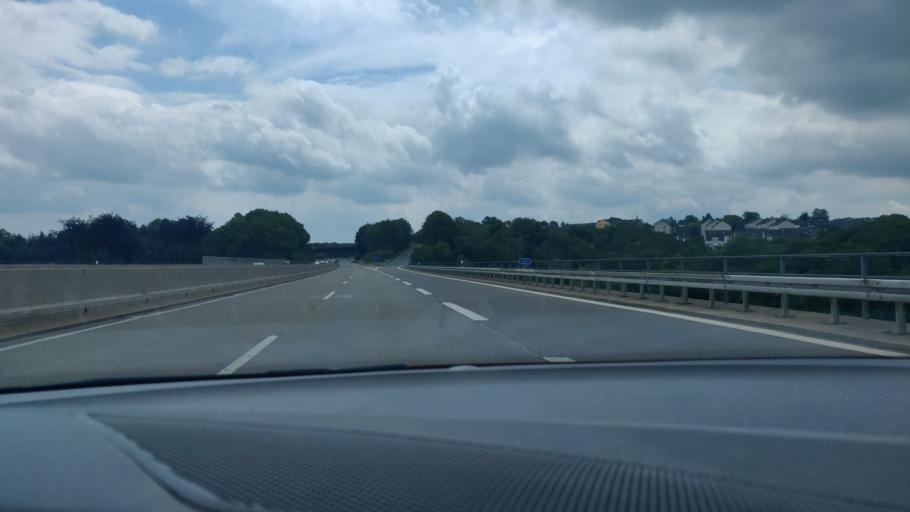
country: DE
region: North Rhine-Westphalia
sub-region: Regierungsbezirk Dusseldorf
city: Velbert
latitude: 51.3225
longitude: 7.0685
